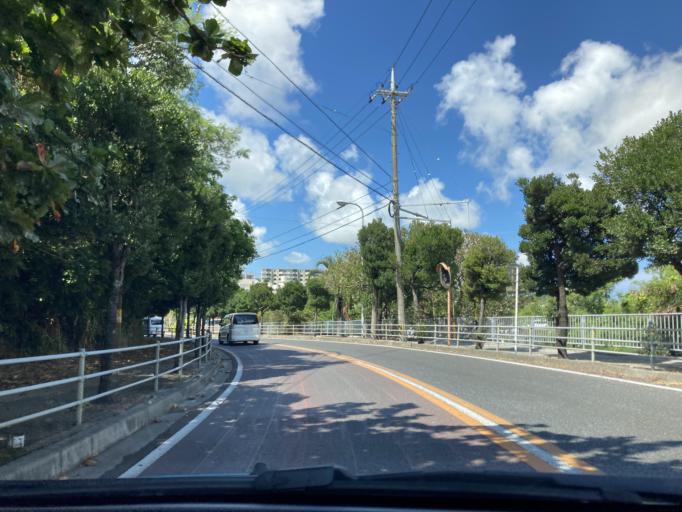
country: JP
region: Okinawa
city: Tomigusuku
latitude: 26.1730
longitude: 127.7208
